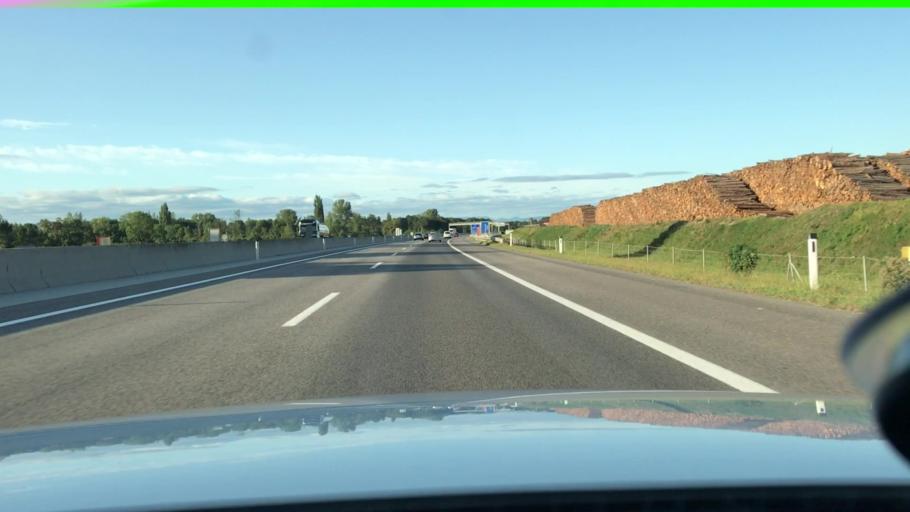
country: AT
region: Lower Austria
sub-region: Politischer Bezirk Sankt Polten
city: Herzogenburg
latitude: 48.2564
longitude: 15.6944
